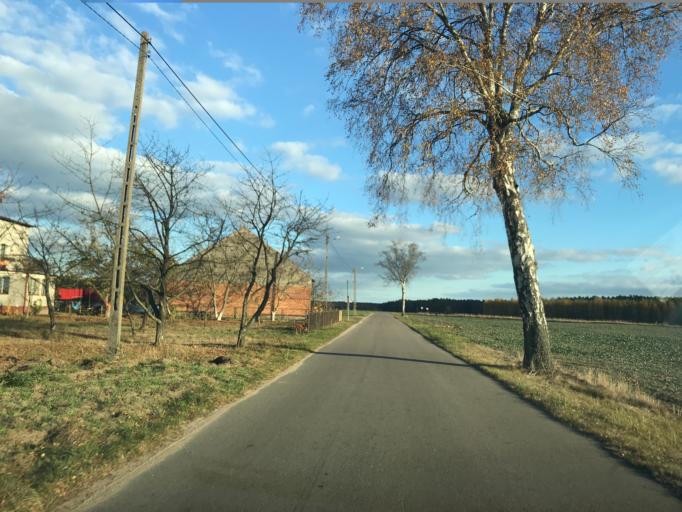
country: PL
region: Warmian-Masurian Voivodeship
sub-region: Powiat dzialdowski
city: Rybno
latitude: 53.3745
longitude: 19.8325
